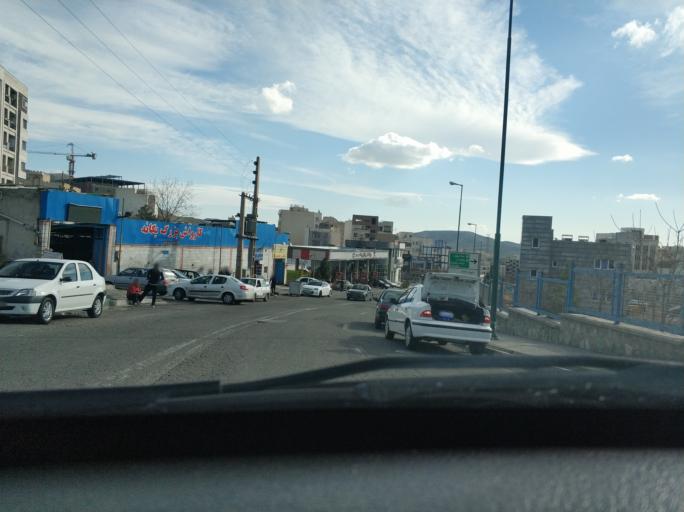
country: IR
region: Tehran
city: Tehran
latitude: 35.7424
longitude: 51.5941
